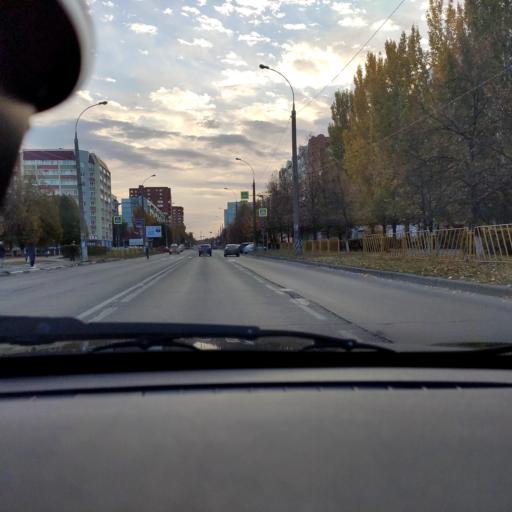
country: RU
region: Samara
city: Tol'yatti
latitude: 53.5333
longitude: 49.3319
